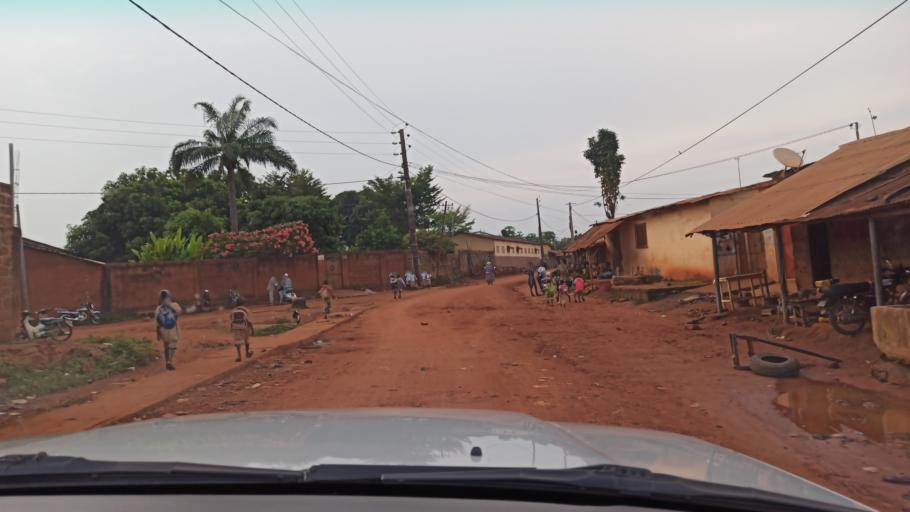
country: BJ
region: Queme
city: Porto-Novo
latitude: 6.5298
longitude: 2.6650
